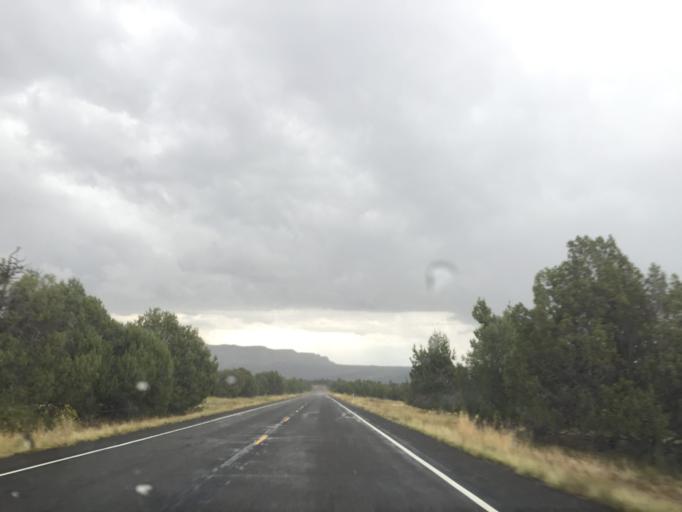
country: US
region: Utah
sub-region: Kane County
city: Kanab
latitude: 37.2251
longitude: -112.7217
